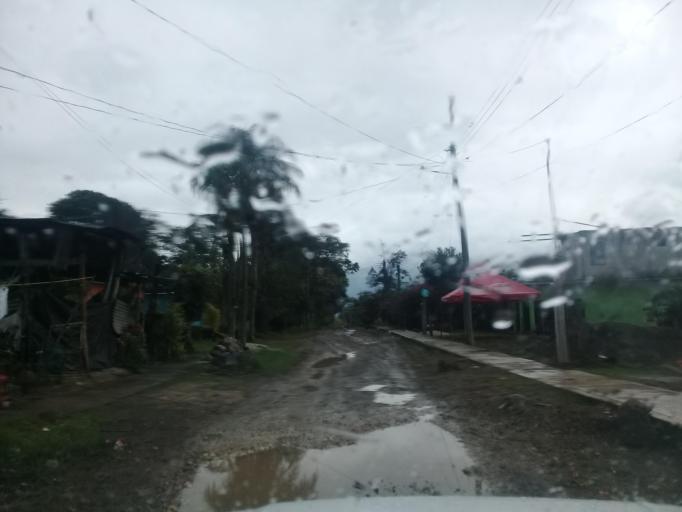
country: MX
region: Veracruz
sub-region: Amatlan de los Reyes
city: Trapiche Viejo
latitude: 18.8413
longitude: -96.9474
